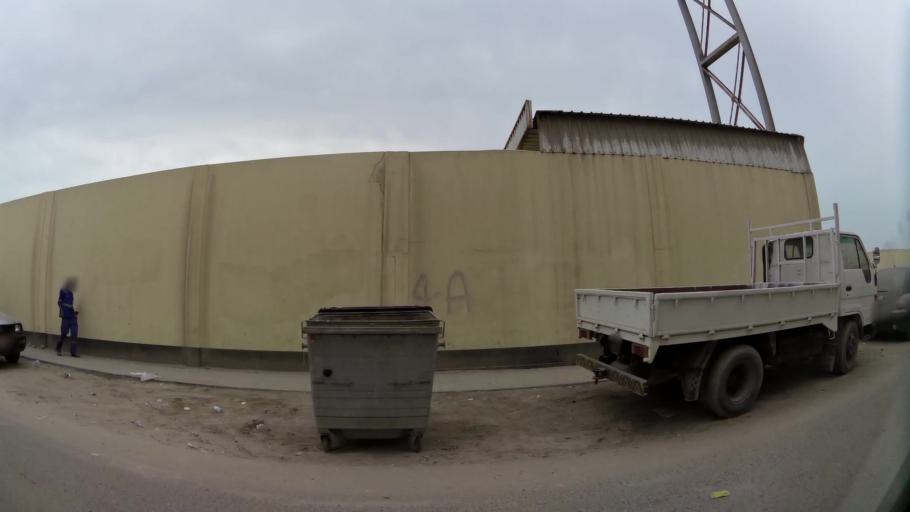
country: BH
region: Northern
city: Madinat `Isa
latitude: 26.1794
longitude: 50.5254
